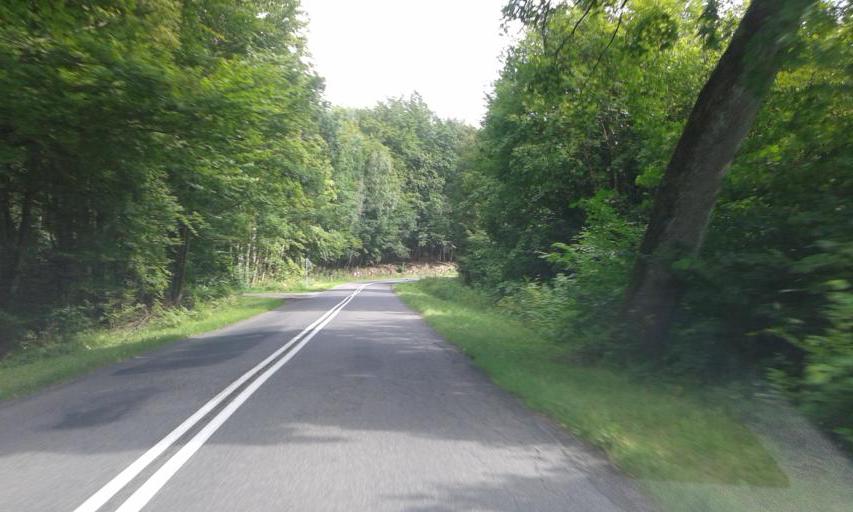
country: PL
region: West Pomeranian Voivodeship
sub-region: Powiat koszalinski
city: Bobolice
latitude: 53.9714
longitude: 16.6540
